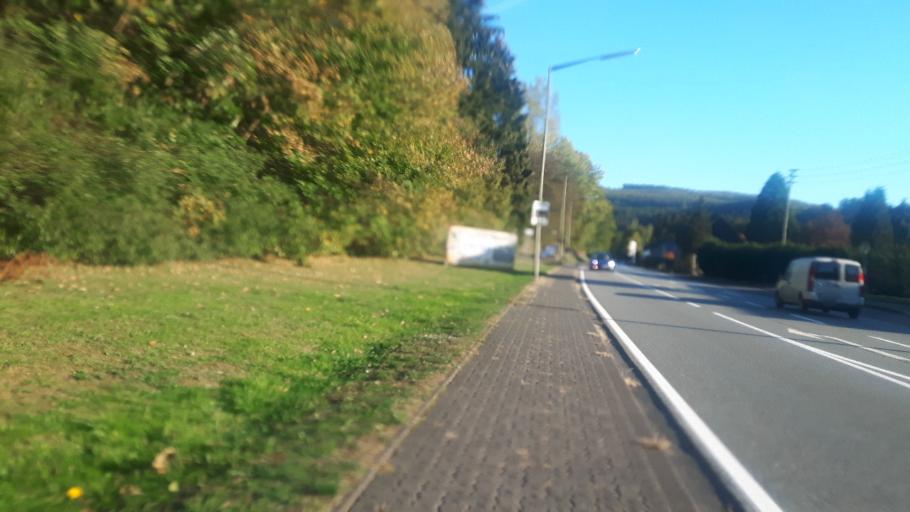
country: DE
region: Rheinland-Pfalz
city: Kirchen
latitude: 50.8222
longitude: 7.8880
